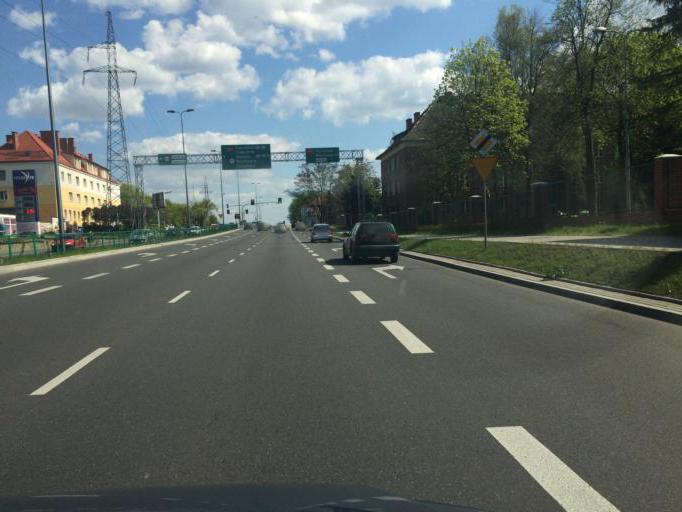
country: PL
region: Warmian-Masurian Voivodeship
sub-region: Olsztyn
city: Kortowo
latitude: 53.7674
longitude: 20.4630
